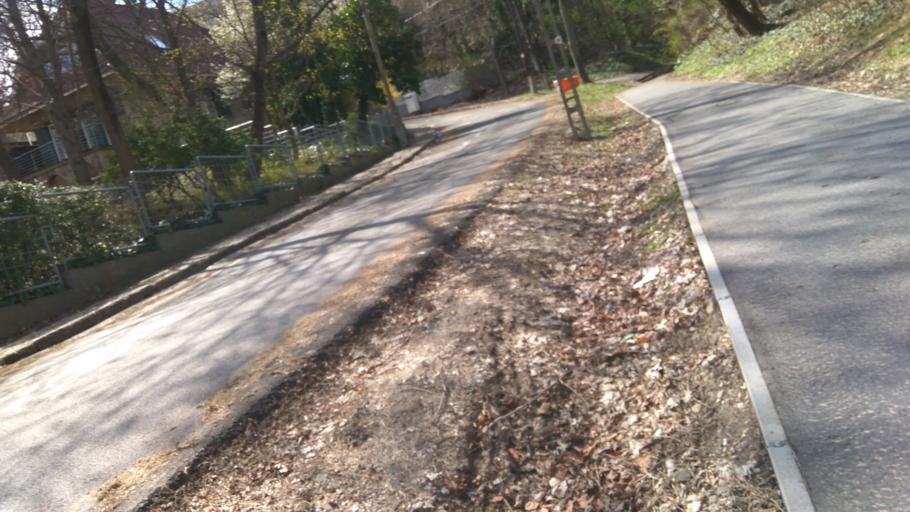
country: HU
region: Budapest
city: Budapest XII. keruelet
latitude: 47.4995
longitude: 19.0041
